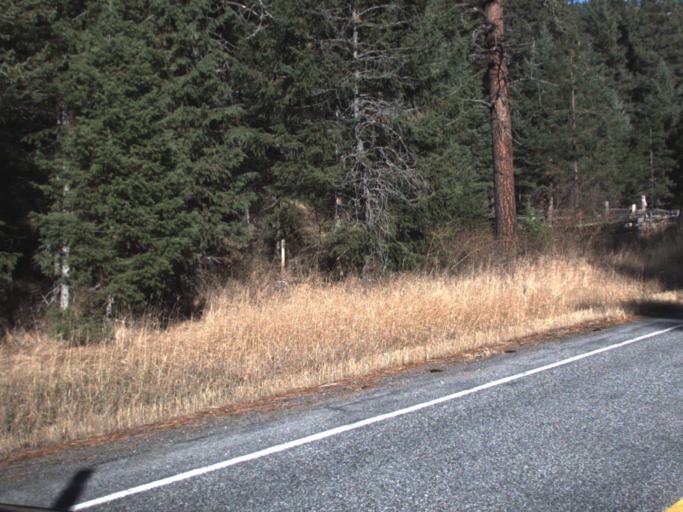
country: US
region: Washington
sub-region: Ferry County
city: Republic
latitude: 48.5999
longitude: -118.7394
